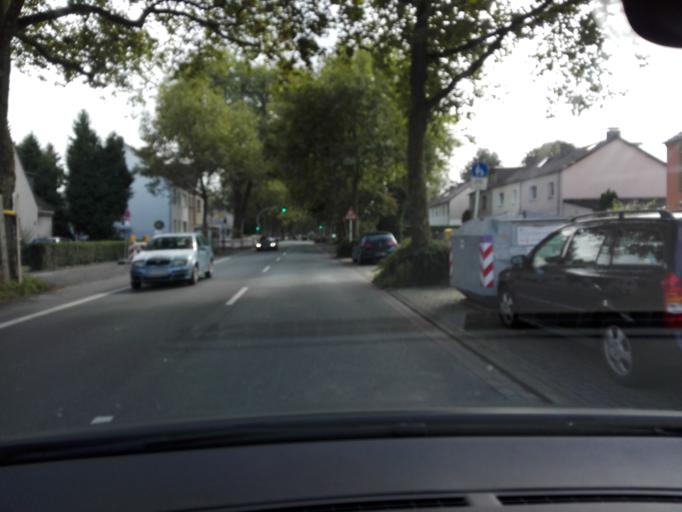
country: DE
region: North Rhine-Westphalia
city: Lanstrop
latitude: 51.5322
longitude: 7.5447
